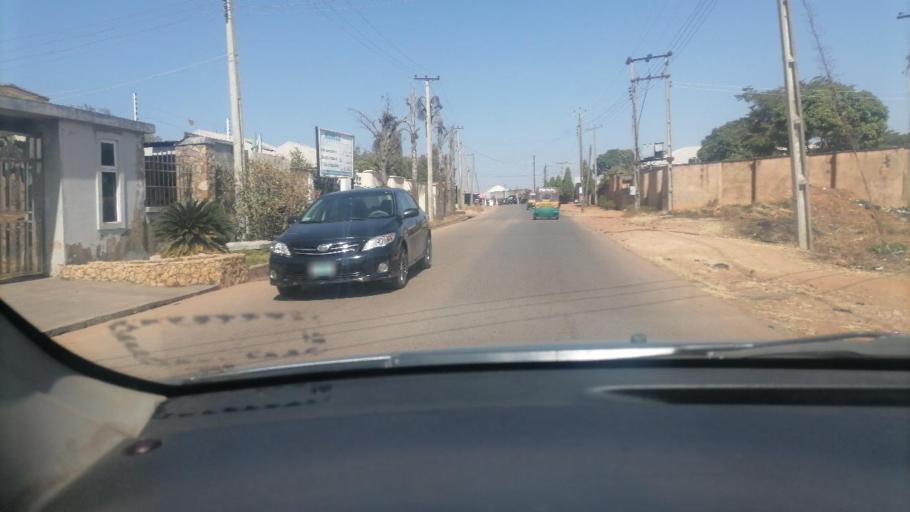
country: NG
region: Plateau
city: Jos
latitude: 9.8699
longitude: 8.9067
